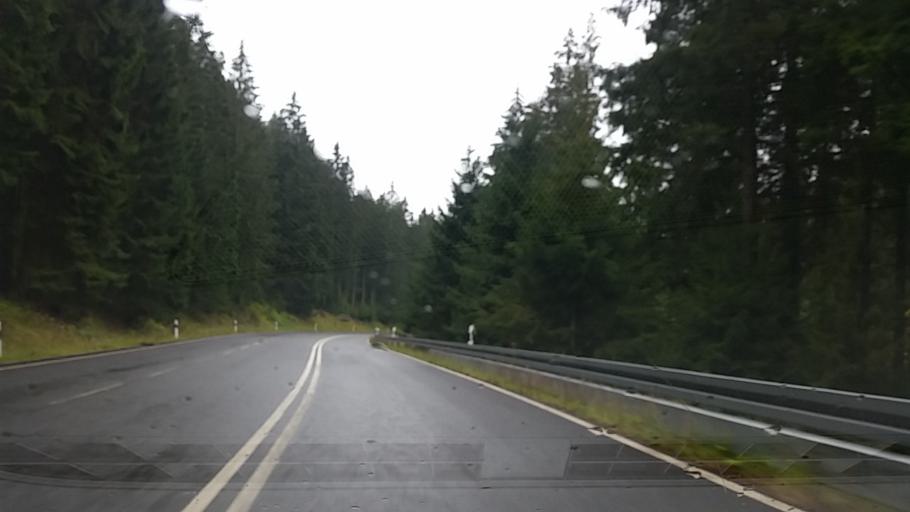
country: DE
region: Lower Saxony
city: Altenau
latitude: 51.7735
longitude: 10.4091
